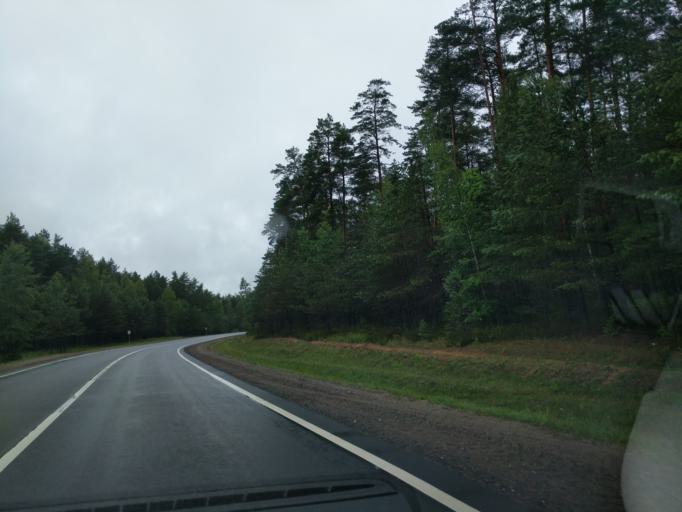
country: BY
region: Minsk
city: Syomkava
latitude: 54.1991
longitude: 27.4959
